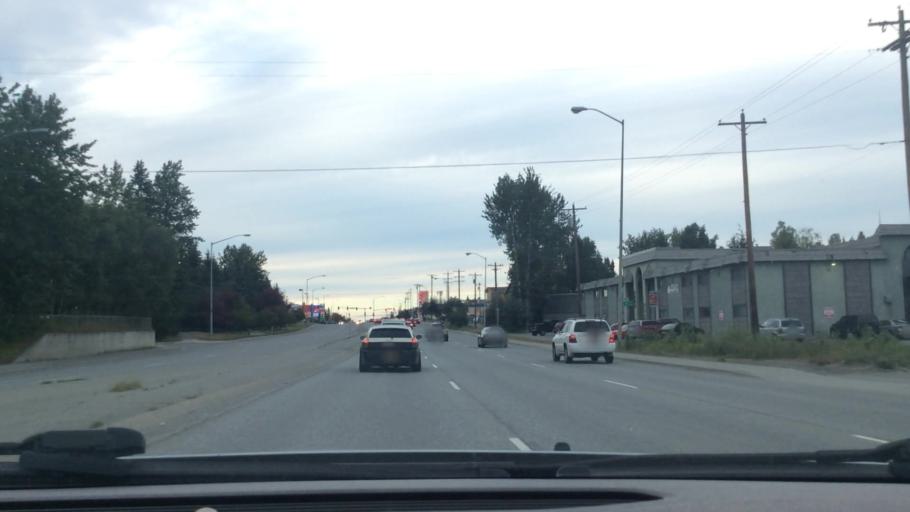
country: US
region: Alaska
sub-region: Anchorage Municipality
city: Anchorage
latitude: 61.1833
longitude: -149.9130
